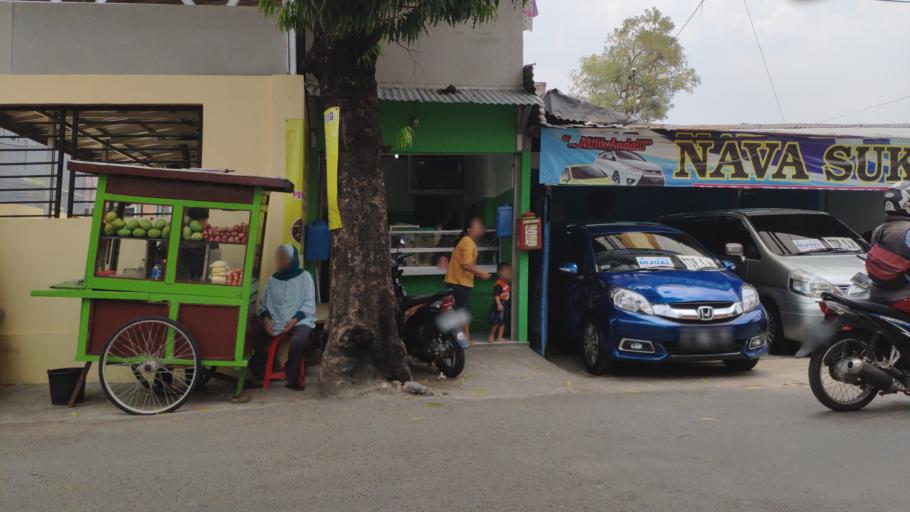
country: ID
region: Jakarta Raya
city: Jakarta
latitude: -6.2668
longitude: 106.7924
